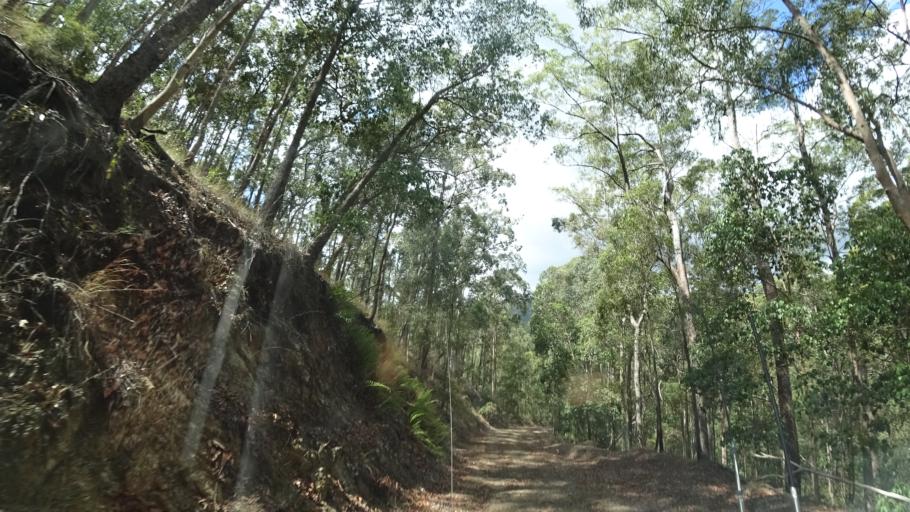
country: AU
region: Queensland
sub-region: Moreton Bay
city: Highvale
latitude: -27.3439
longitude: 152.7278
